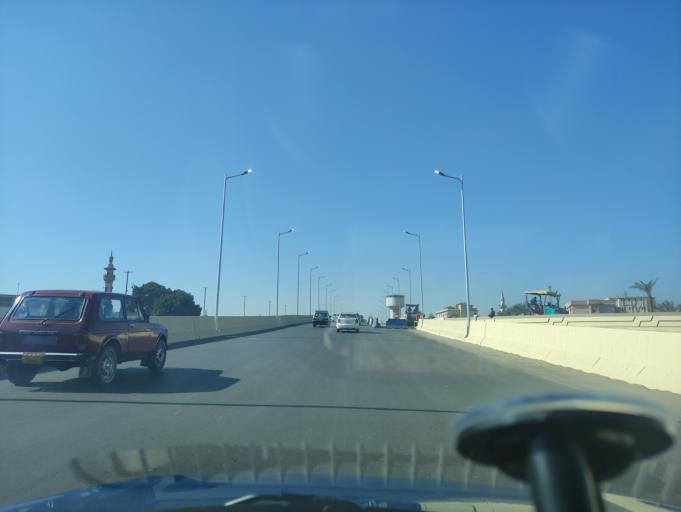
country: EG
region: Muhafazat al Qahirah
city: Cairo
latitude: 30.0572
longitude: 31.2808
